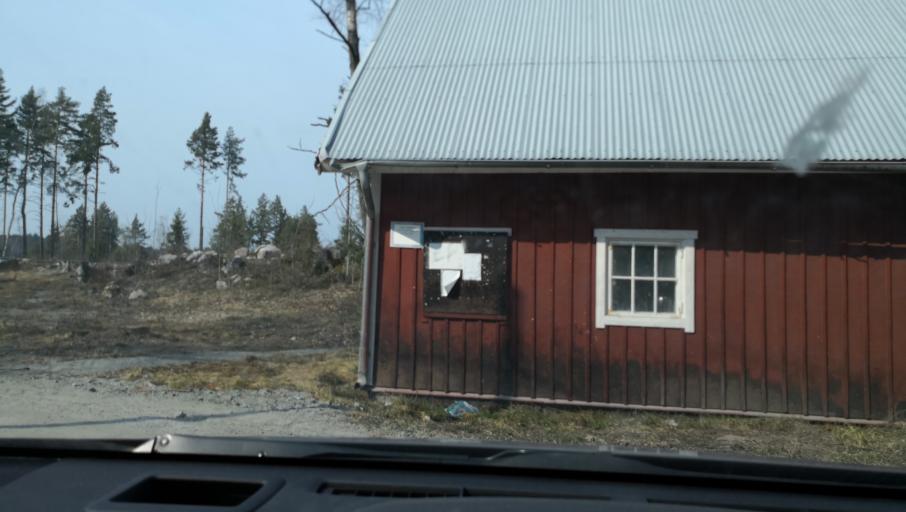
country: SE
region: OErebro
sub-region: Lindesbergs Kommun
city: Frovi
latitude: 59.3901
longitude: 15.4038
